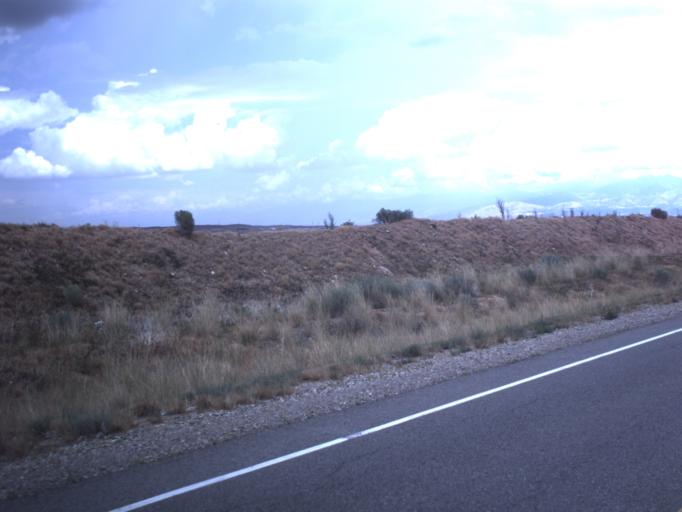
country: US
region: Utah
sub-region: Salt Lake County
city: Herriman
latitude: 40.5694
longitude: -112.0755
